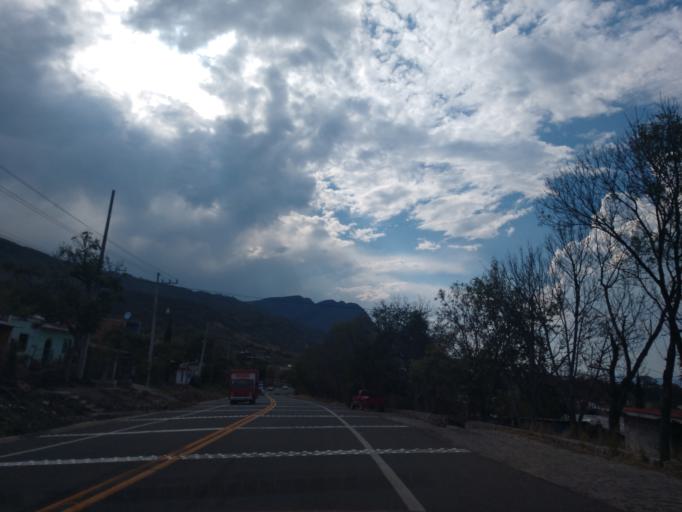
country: MX
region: Jalisco
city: Chapala
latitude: 20.1697
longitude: -103.2110
